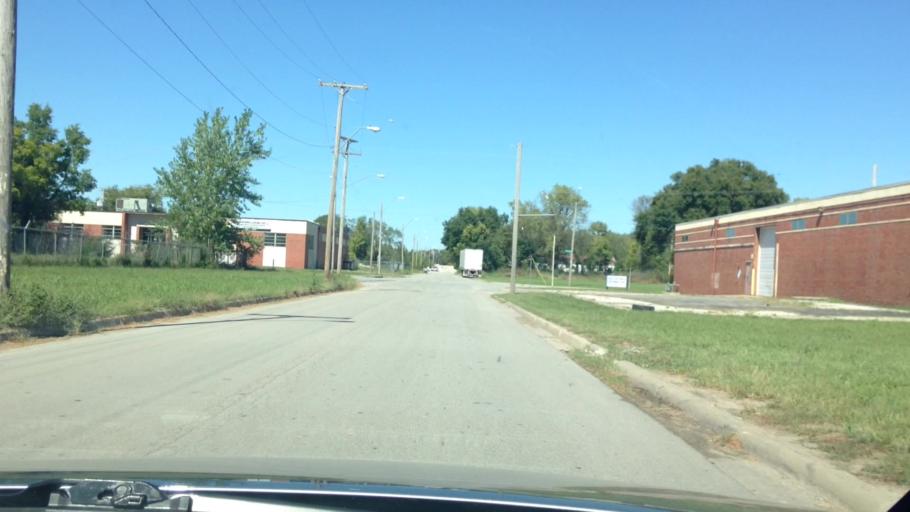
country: US
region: Missouri
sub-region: Jackson County
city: Raytown
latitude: 39.0175
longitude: -94.5259
